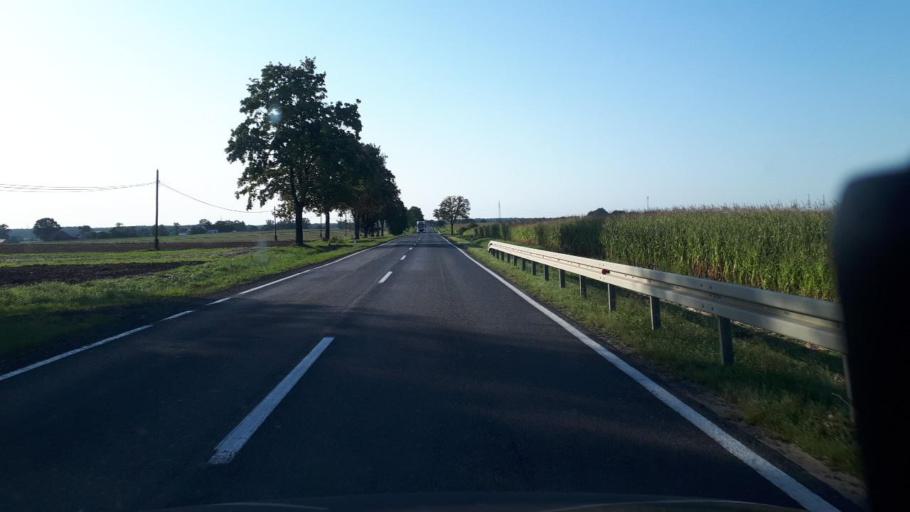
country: PL
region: Silesian Voivodeship
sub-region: Powiat lubliniecki
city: Sierakow Slaski
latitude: 50.8372
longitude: 18.5092
